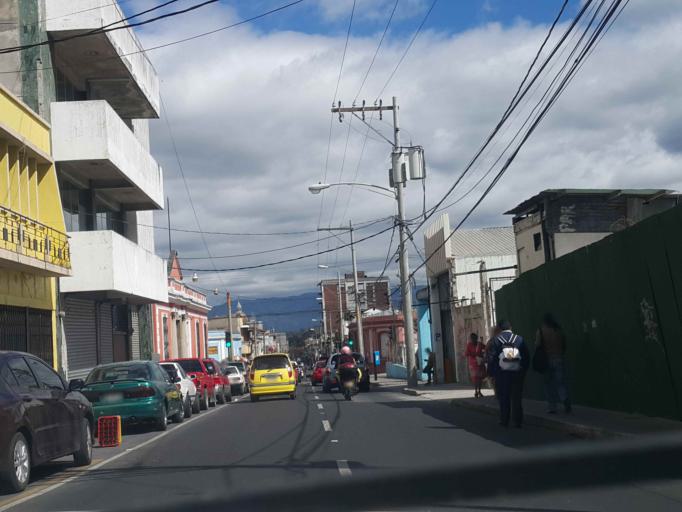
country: GT
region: Guatemala
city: Guatemala City
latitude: 14.6432
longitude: -90.5122
